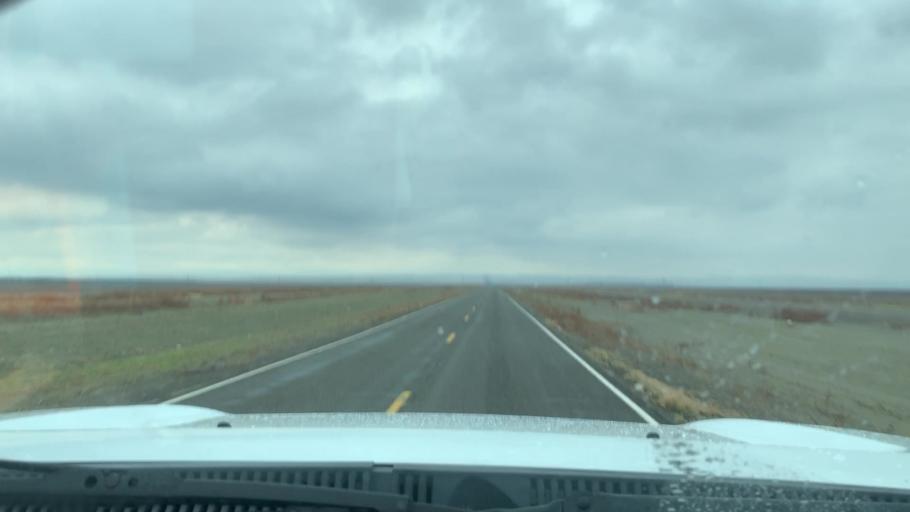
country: US
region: California
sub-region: Kings County
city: Kettleman City
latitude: 35.9340
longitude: -119.8326
